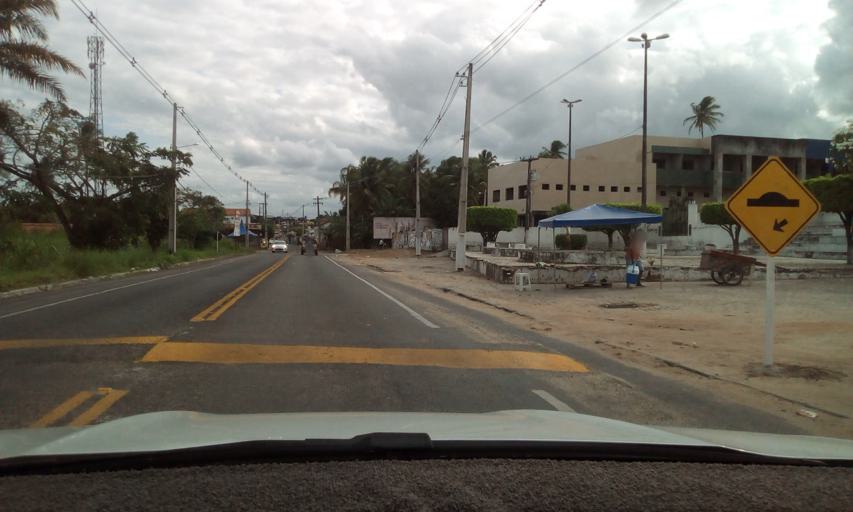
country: BR
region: Paraiba
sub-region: Mamanguape
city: Mamanguape
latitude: -6.8324
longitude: -35.1169
